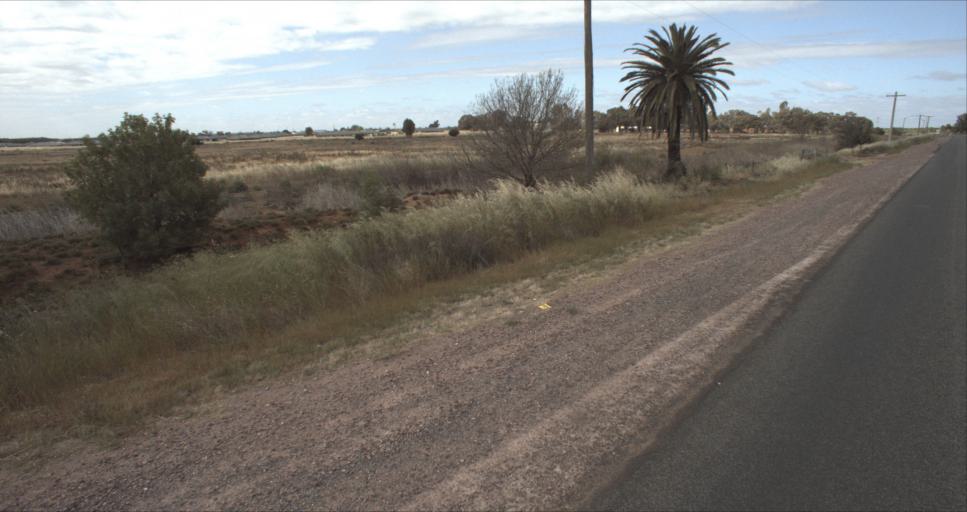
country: AU
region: New South Wales
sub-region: Leeton
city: Leeton
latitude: -34.5663
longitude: 146.3969
